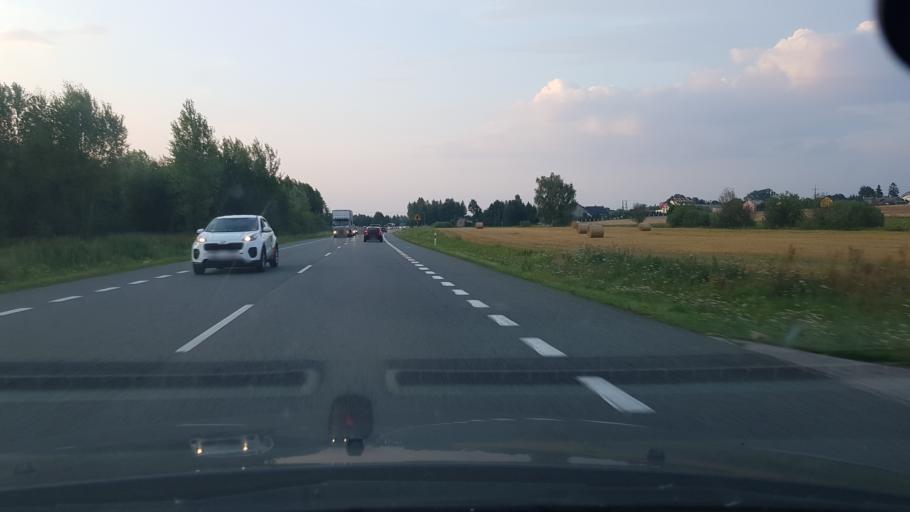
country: PL
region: Masovian Voivodeship
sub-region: Powiat mlawski
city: Wieczfnia Koscielna
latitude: 53.1839
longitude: 20.4302
